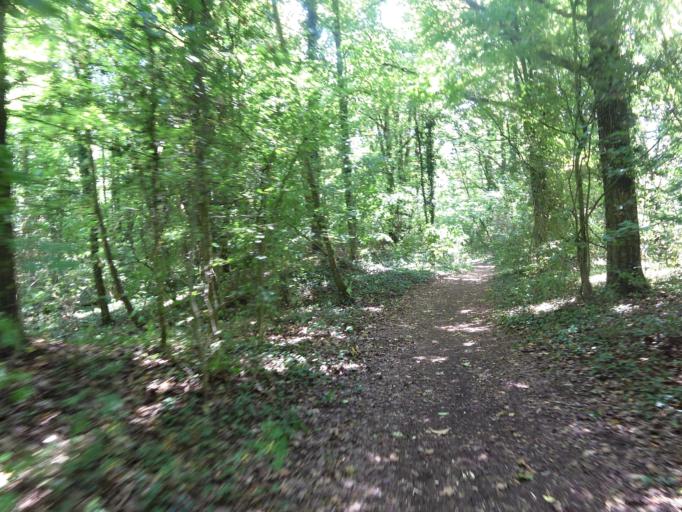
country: DE
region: Bavaria
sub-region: Regierungsbezirk Unterfranken
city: Randersacker
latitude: 49.7439
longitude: 9.9511
